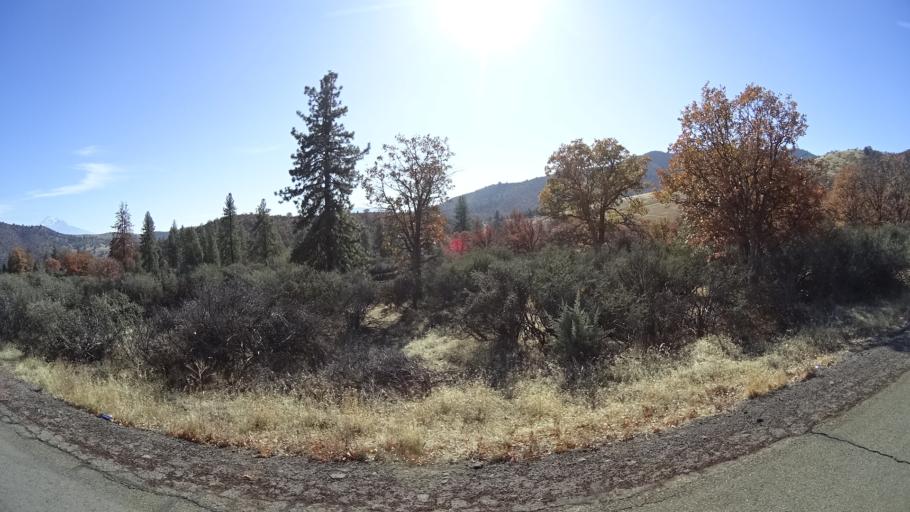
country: US
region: California
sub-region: Siskiyou County
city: Yreka
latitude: 41.7688
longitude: -122.6343
